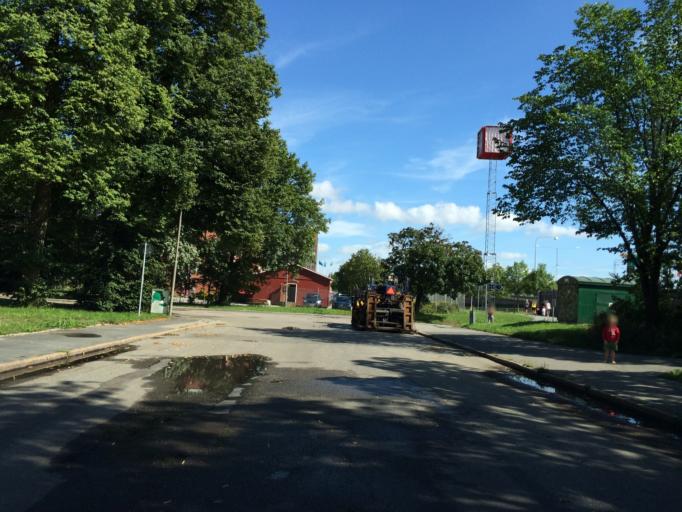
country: SE
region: Stockholm
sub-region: Stockholms Kommun
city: Arsta
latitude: 59.2939
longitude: 17.9992
